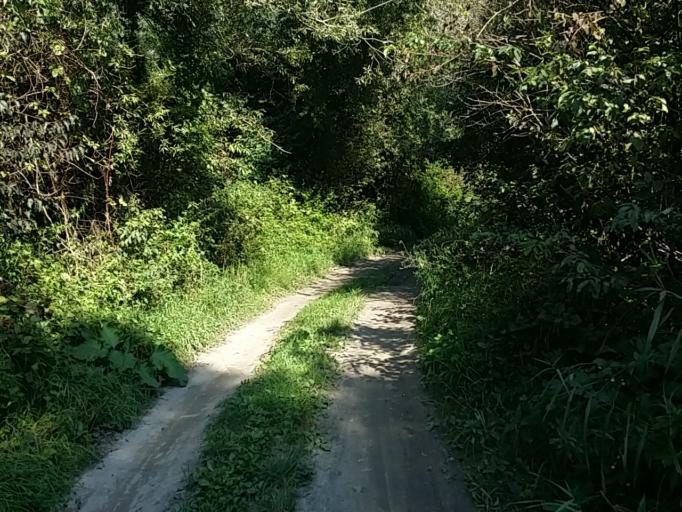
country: HR
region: Koprivnicko-Krizevacka
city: Ferdinandovac
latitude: 46.1149
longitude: 17.2082
